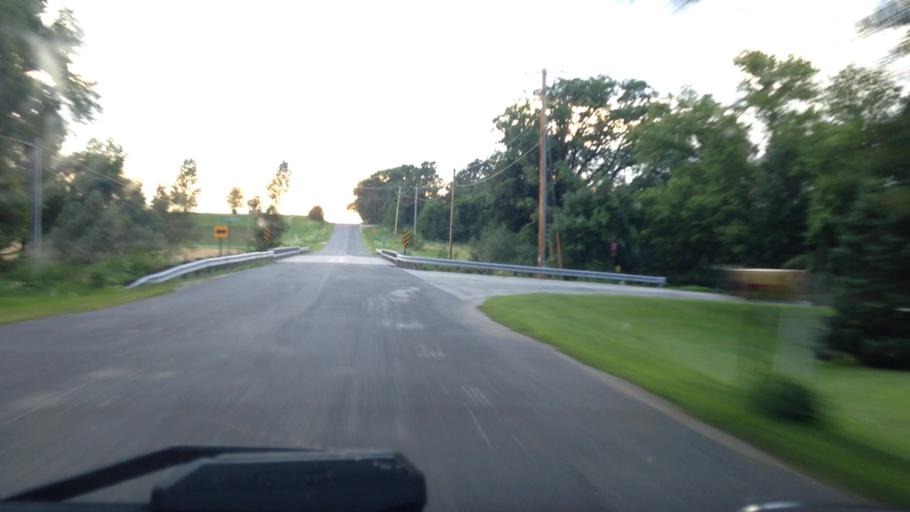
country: US
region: Wisconsin
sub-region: Dodge County
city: Mayville
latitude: 43.4932
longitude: -88.5102
